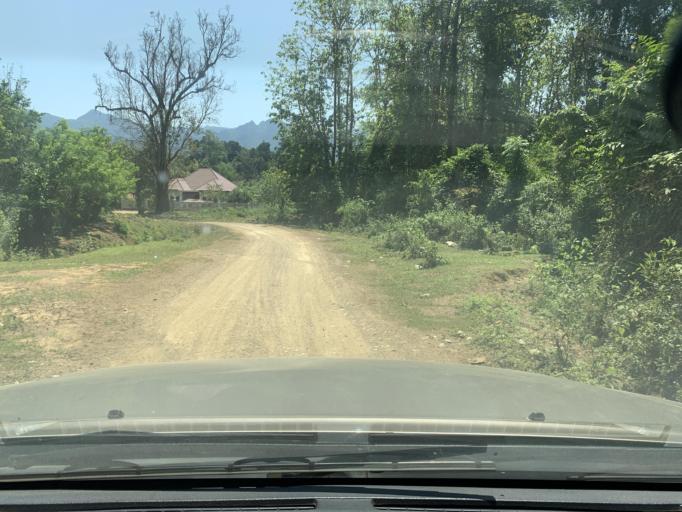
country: LA
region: Louangphabang
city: Louangphabang
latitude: 19.9043
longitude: 102.2260
